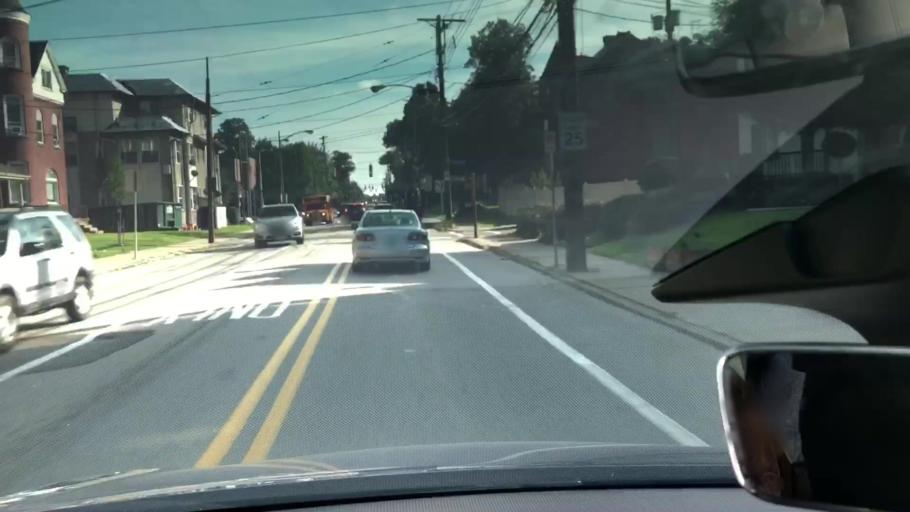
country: US
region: Pennsylvania
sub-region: Allegheny County
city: Bloomfield
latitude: 40.4685
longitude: -79.9277
